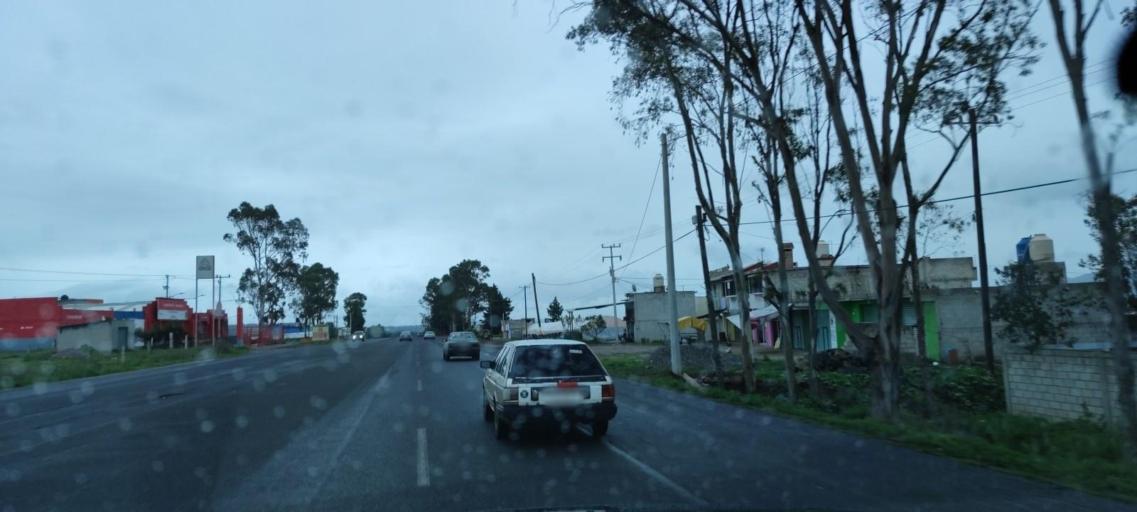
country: MX
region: Mexico
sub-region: Jilotepec
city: Doxhicho
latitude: 19.8942
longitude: -99.6231
